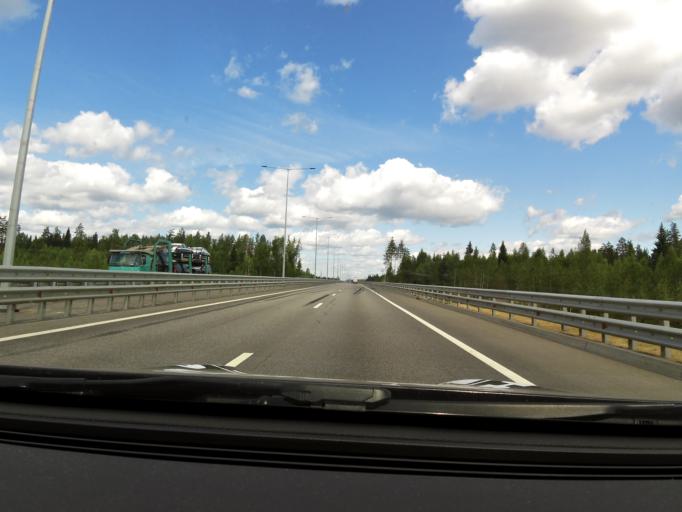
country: RU
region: Tverskaya
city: Krasnomayskiy
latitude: 57.5359
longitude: 34.2736
